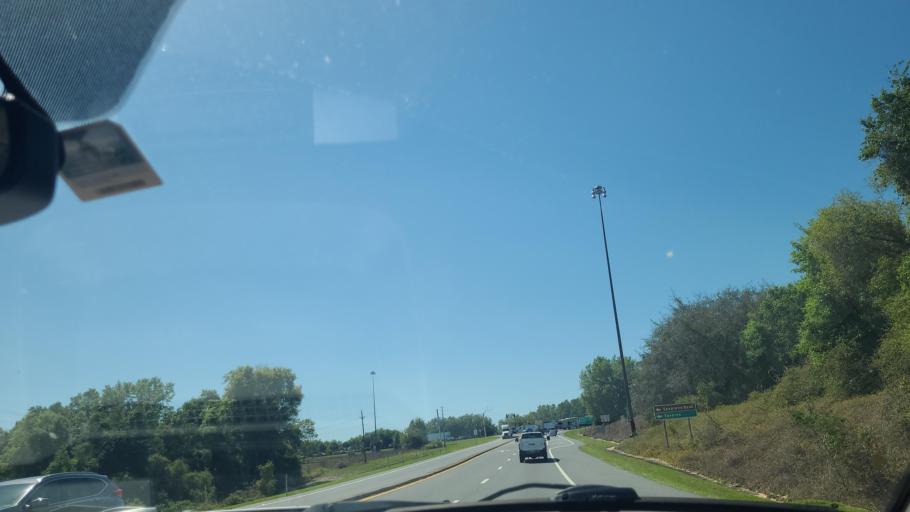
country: US
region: Florida
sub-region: Lake County
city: Howie In The Hills
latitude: 28.6456
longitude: -81.8093
